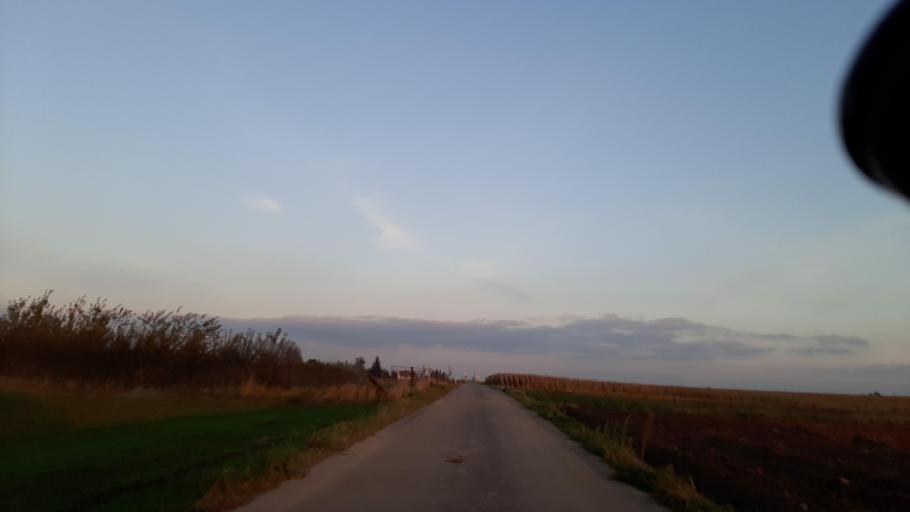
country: PL
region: Lublin Voivodeship
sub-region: Powiat lubelski
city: Garbow
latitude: 51.3582
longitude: 22.3913
